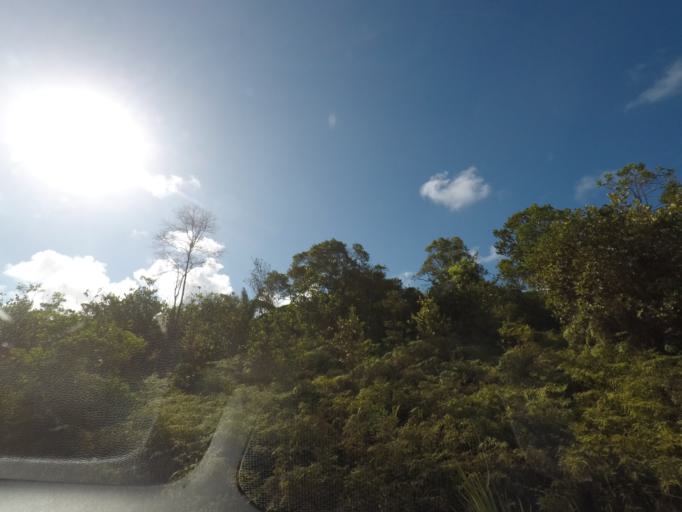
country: BR
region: Bahia
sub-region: Marau
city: Marau
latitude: -14.1077
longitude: -38.9817
